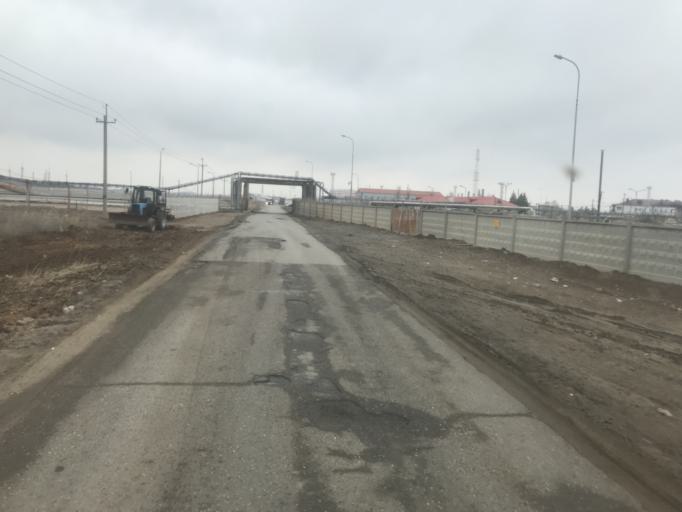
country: RU
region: Volgograd
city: Svetlyy Yar
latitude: 48.5078
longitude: 44.6420
